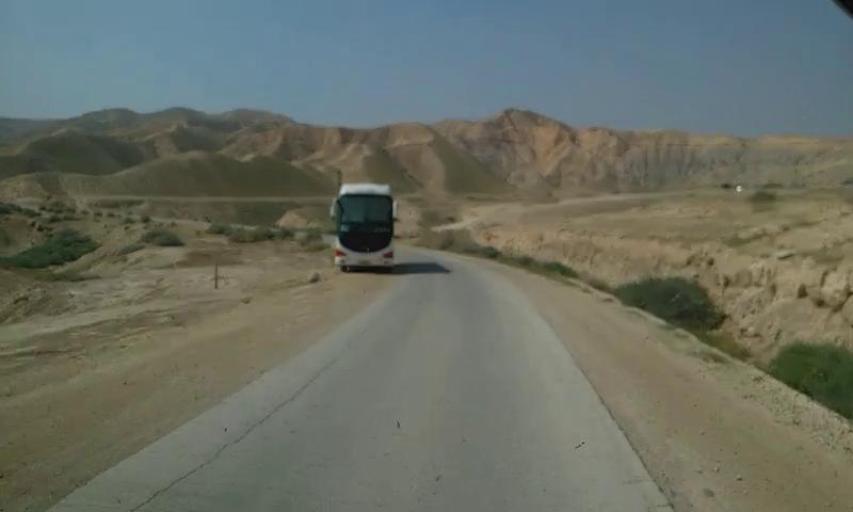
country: PS
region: West Bank
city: Jericho
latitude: 31.7806
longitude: 35.4183
